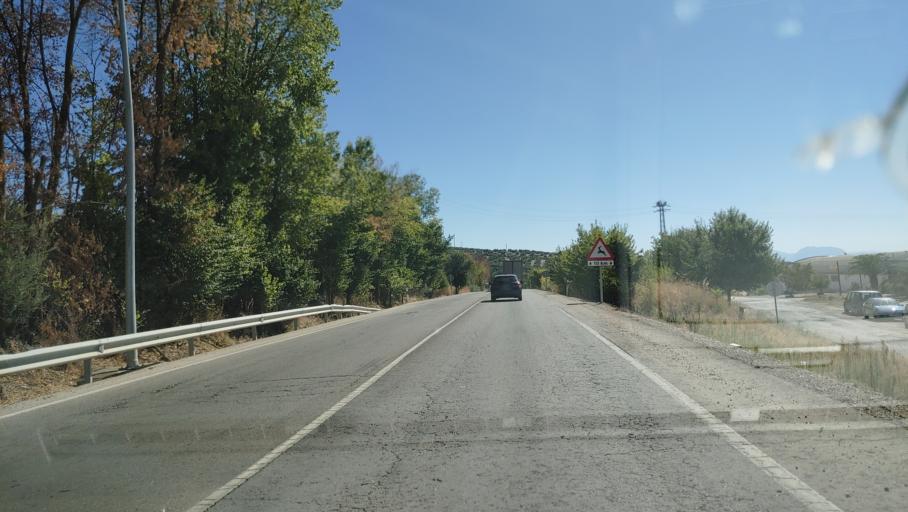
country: ES
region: Andalusia
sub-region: Provincia de Jaen
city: Villacarrillo
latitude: 38.1106
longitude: -3.0980
